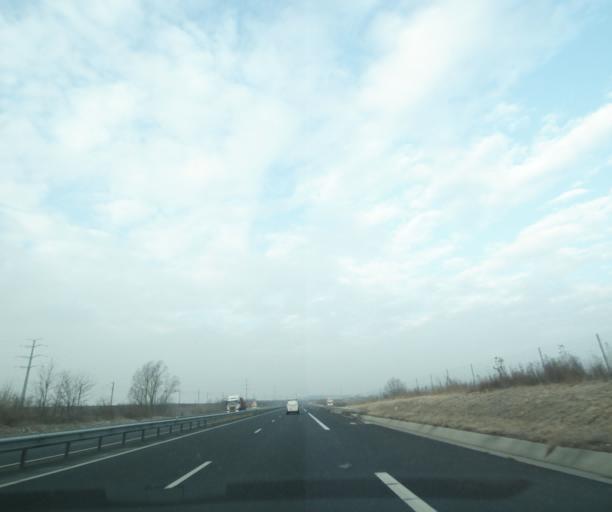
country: FR
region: Rhone-Alpes
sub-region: Departement de l'Ain
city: Mionnay
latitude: 45.8581
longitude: 4.9215
